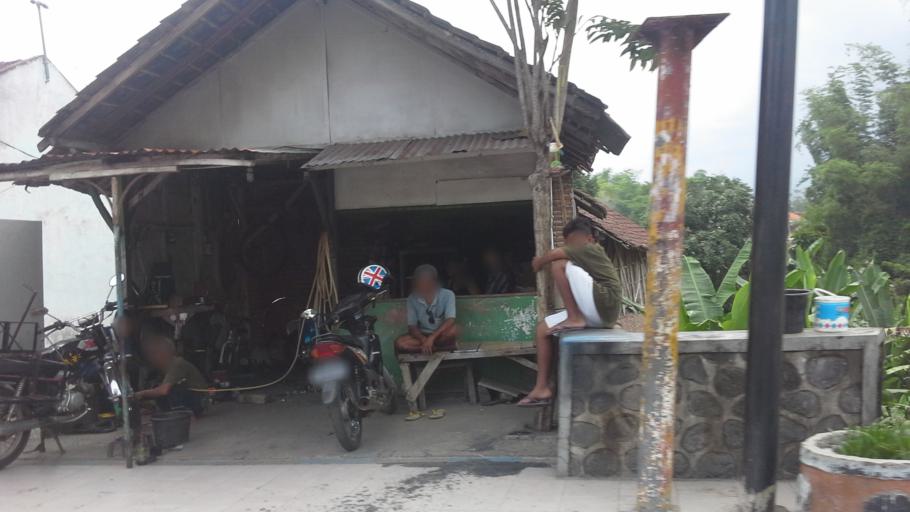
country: ID
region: East Java
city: Bondowoso
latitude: -7.9158
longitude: 113.8286
